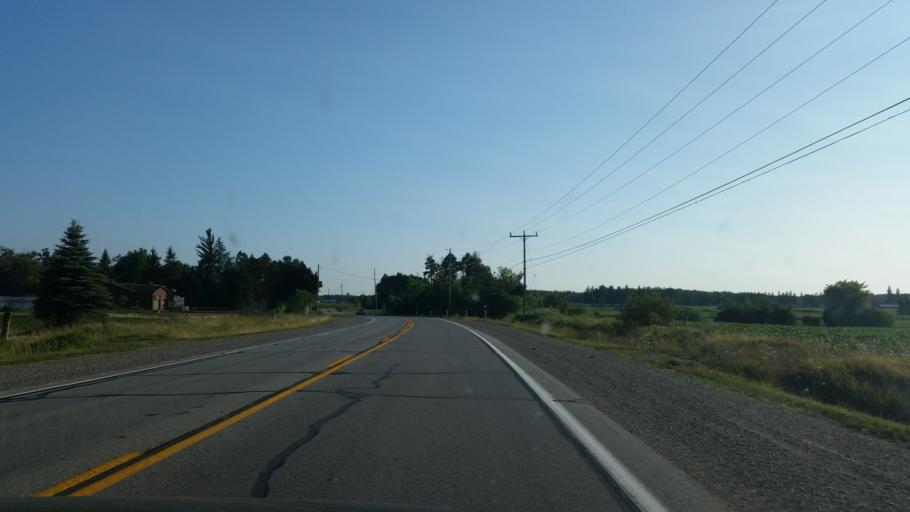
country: CA
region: Ontario
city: Brampton
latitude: 43.8188
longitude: -79.8294
